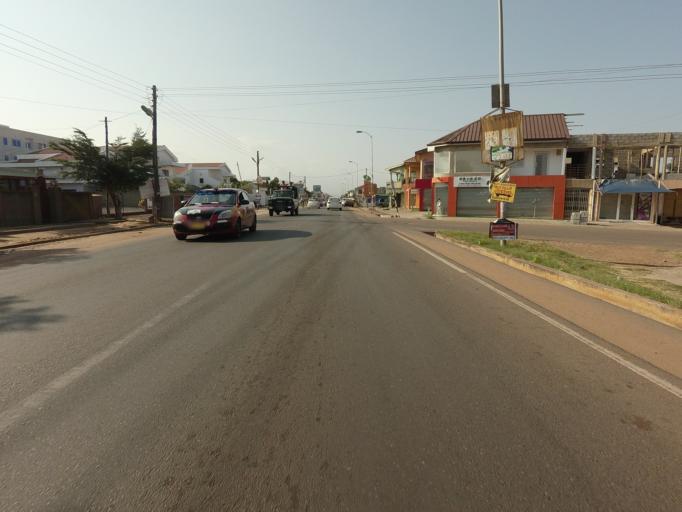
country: GH
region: Greater Accra
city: Nungua
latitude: 5.6352
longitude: -0.0762
